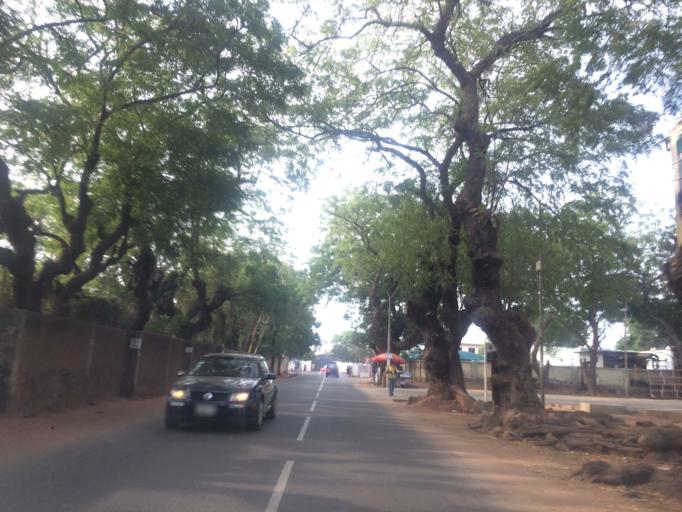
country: GH
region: Greater Accra
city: Accra
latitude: 5.5366
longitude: -0.2295
